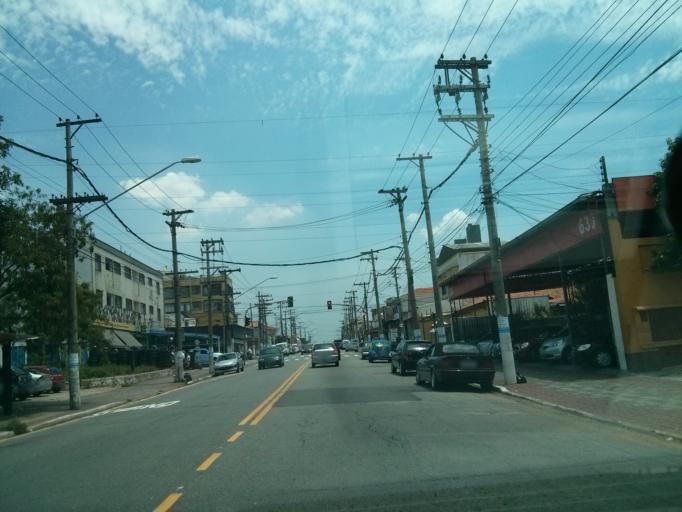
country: BR
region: Sao Paulo
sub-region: Sao Paulo
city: Sao Paulo
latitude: -23.6076
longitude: -46.6168
